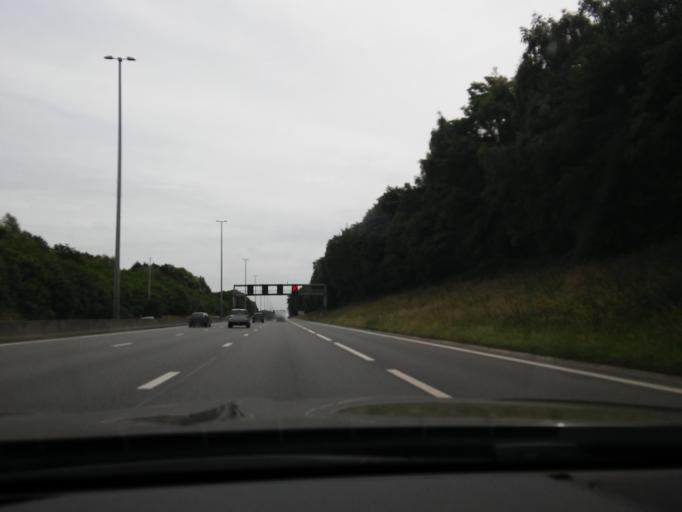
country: BE
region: Flanders
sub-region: Provincie Vlaams-Brabant
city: Kortenberg
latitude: 50.8693
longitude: 4.5262
